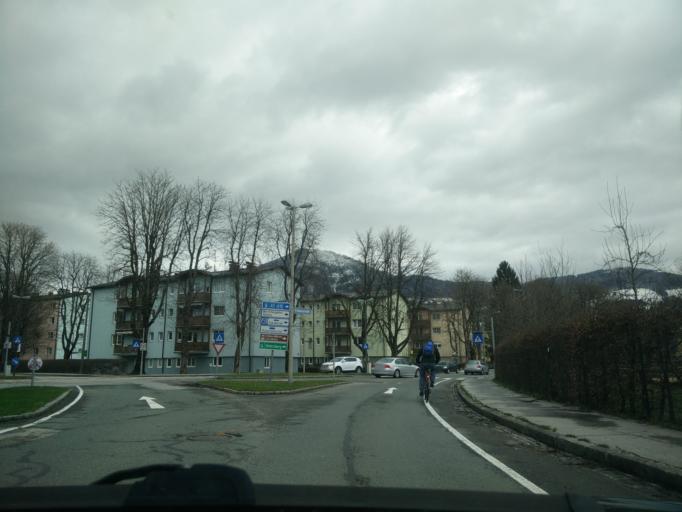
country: AT
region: Salzburg
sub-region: Salzburg Stadt
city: Salzburg
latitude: 47.7859
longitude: 13.0600
